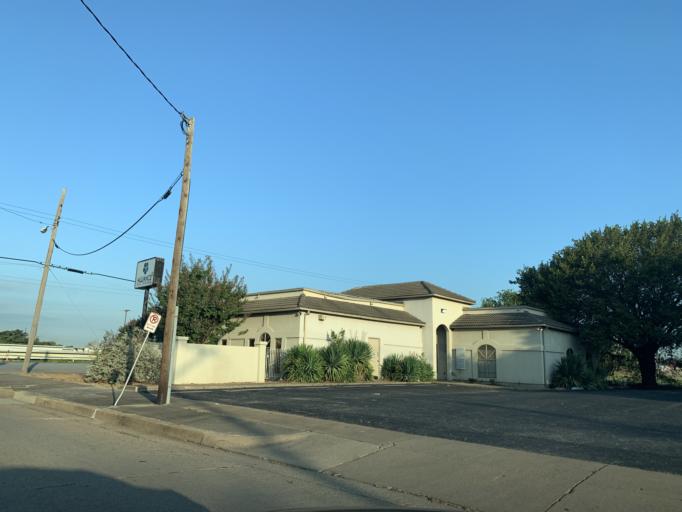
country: US
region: Texas
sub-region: Tarrant County
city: Fort Worth
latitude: 32.7656
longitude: -97.3380
